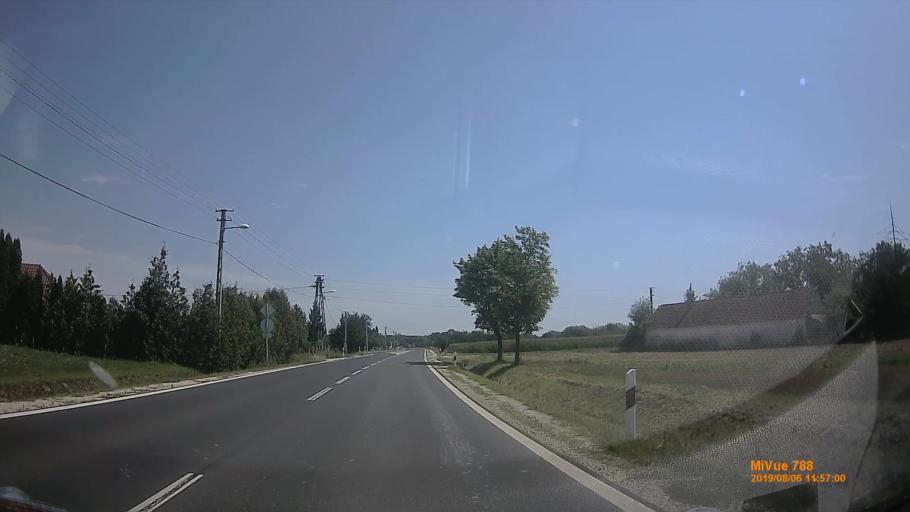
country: HU
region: Vas
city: Vasvar
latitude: 47.0584
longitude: 16.7029
